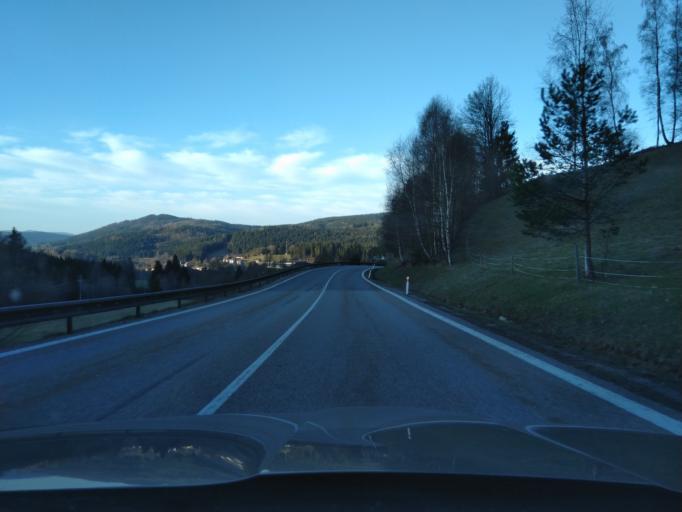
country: CZ
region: Jihocesky
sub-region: Okres Prachatice
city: Vimperk
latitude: 48.9684
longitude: 13.7604
